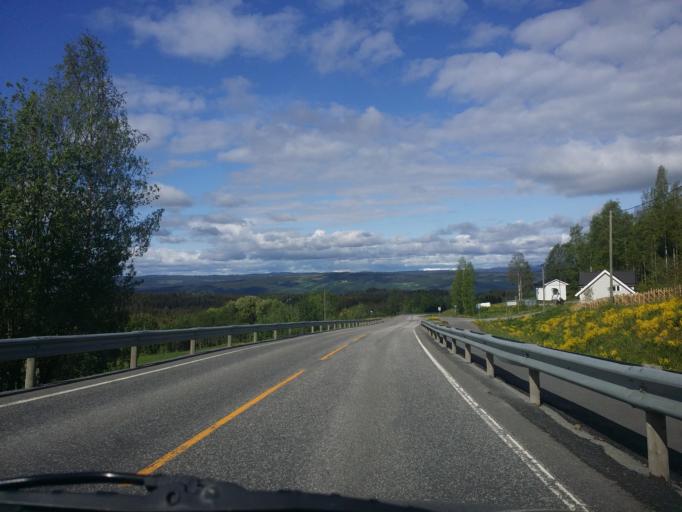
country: NO
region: Oppland
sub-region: Lillehammer
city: Lillehammer
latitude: 61.0962
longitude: 10.5399
